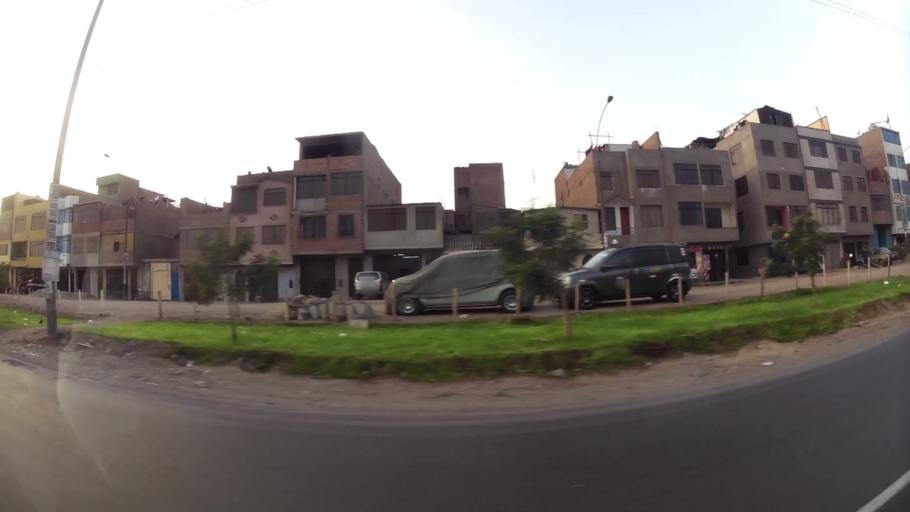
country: PE
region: Lima
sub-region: Lima
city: Independencia
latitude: -12.0119
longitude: -77.0887
